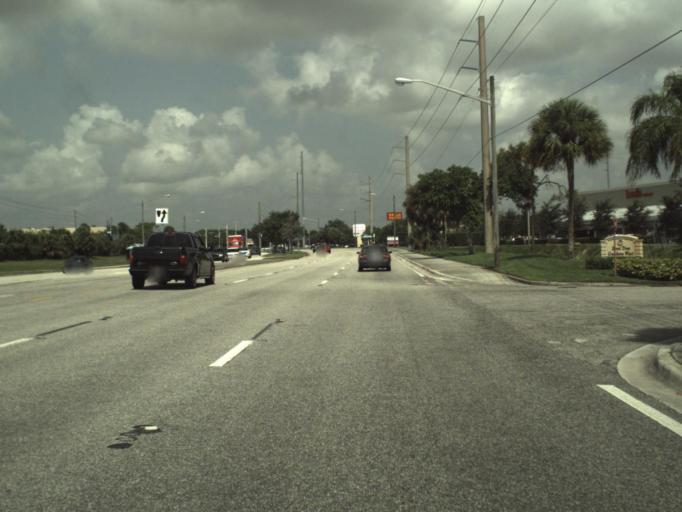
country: US
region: Florida
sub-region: Palm Beach County
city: Boynton Beach
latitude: 26.5277
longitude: -80.1189
